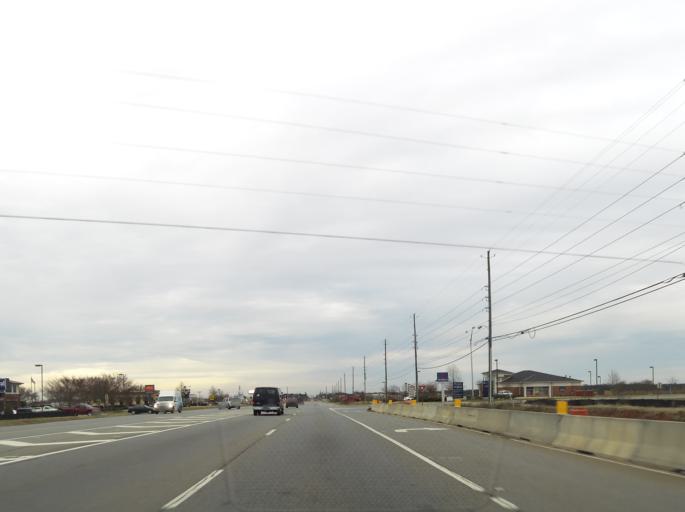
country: US
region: Georgia
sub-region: Houston County
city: Centerville
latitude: 32.5545
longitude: -83.6709
